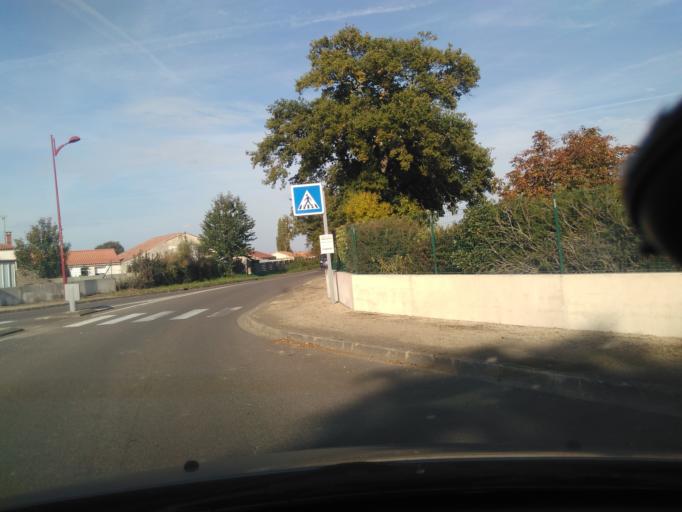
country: FR
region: Pays de la Loire
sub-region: Departement de la Vendee
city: Nieul-le-Dolent
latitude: 46.5760
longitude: -1.4991
